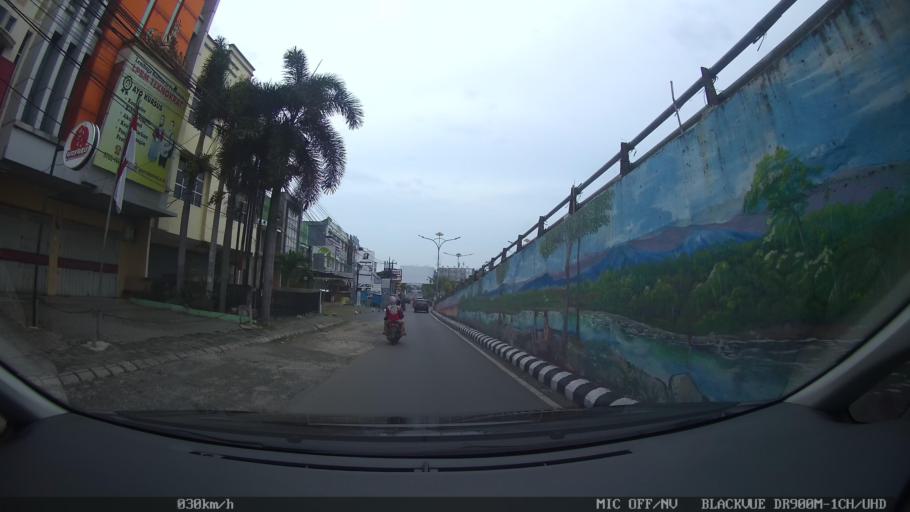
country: ID
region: Lampung
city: Kedaton
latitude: -5.3815
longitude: 105.2579
